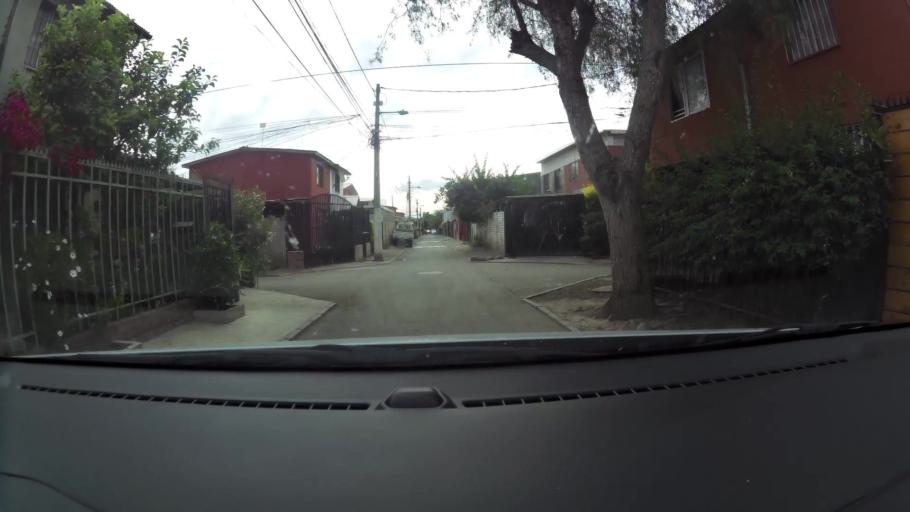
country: CL
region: Santiago Metropolitan
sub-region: Provincia de Cordillera
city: Puente Alto
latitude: -33.6211
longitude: -70.6158
